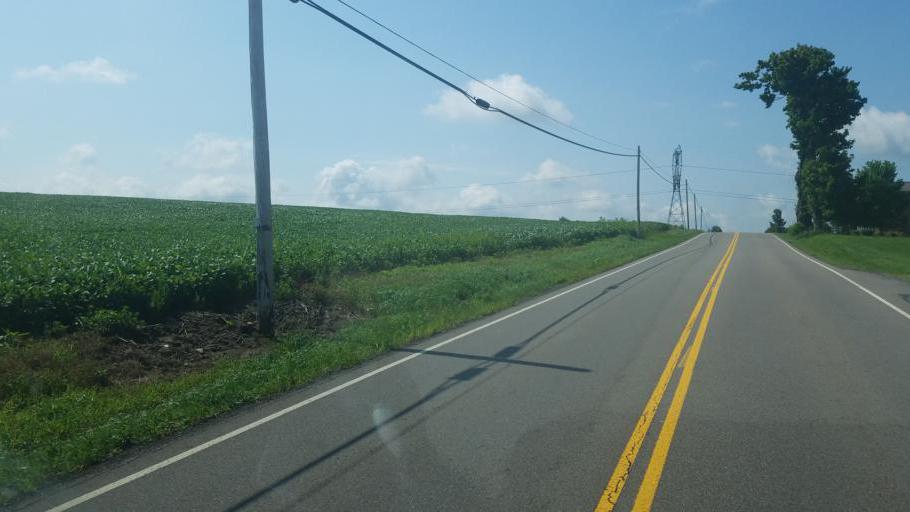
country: US
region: Ohio
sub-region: Licking County
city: Granville
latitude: 40.1011
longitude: -82.5193
